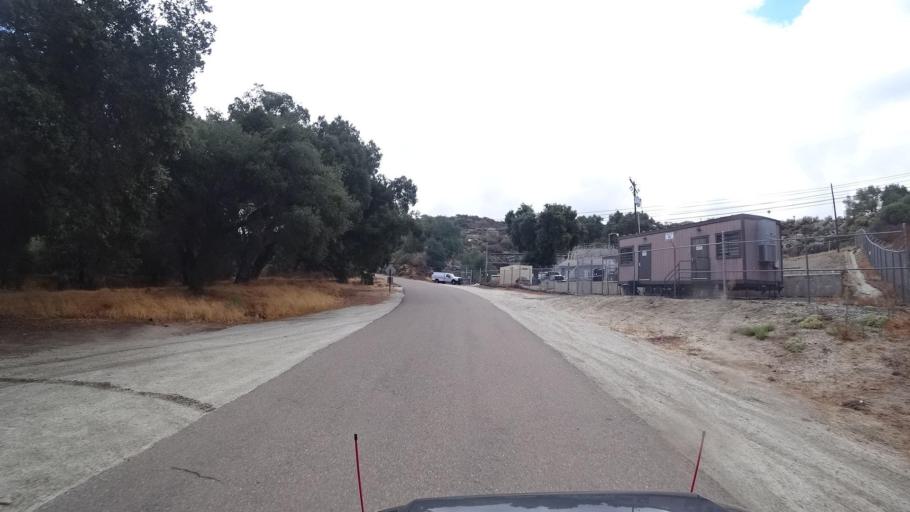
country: US
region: California
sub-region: San Diego County
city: Campo
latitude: 32.6078
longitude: -116.4794
